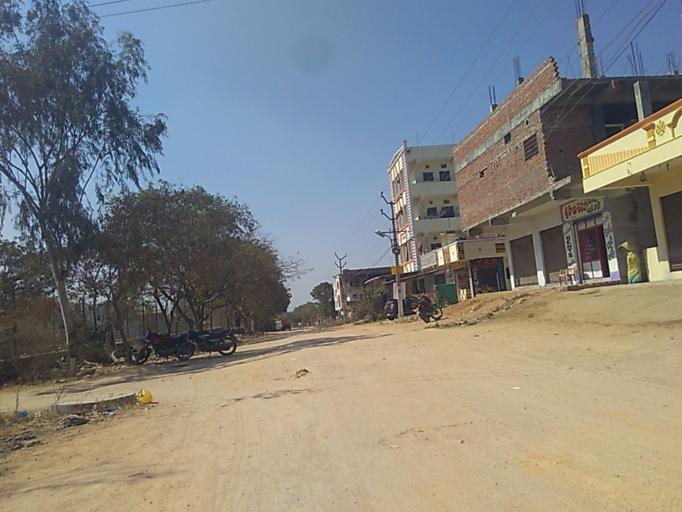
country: IN
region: Telangana
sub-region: Rangareddi
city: Secunderabad
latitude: 17.6265
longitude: 78.5685
